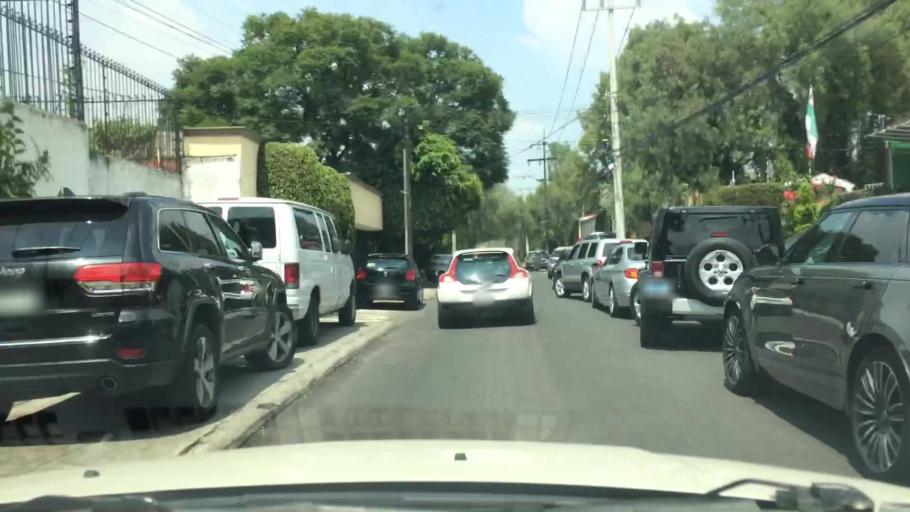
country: MX
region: Mexico City
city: Magdalena Contreras
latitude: 19.3266
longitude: -99.2058
